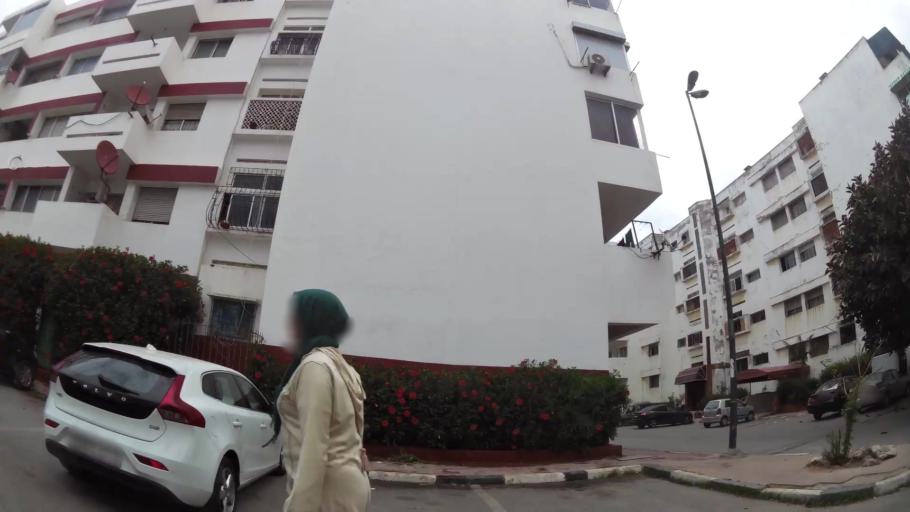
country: MA
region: Rabat-Sale-Zemmour-Zaer
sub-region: Rabat
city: Rabat
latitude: 33.9918
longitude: -6.8817
